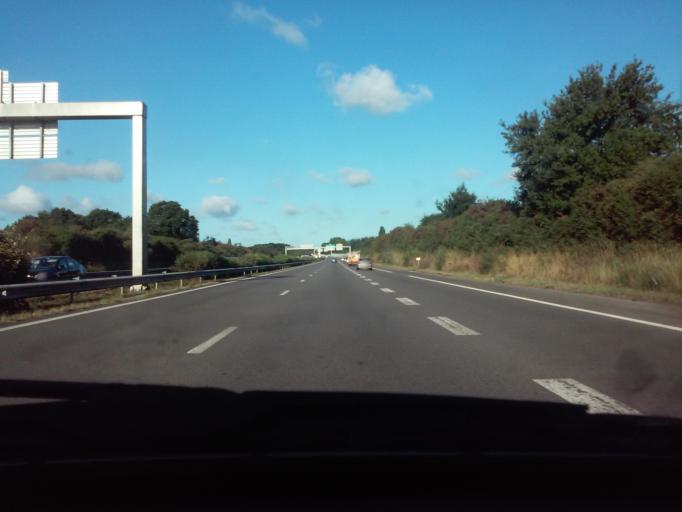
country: FR
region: Pays de la Loire
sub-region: Departement de la Loire-Atlantique
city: Saint-Nazaire
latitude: 47.2900
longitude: -2.2379
